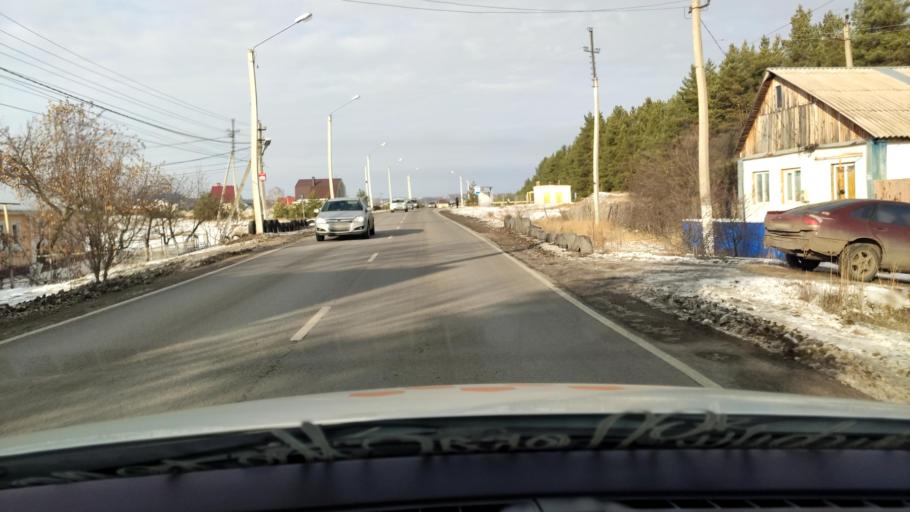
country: RU
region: Voronezj
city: Shilovo
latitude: 51.5826
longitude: 39.0354
